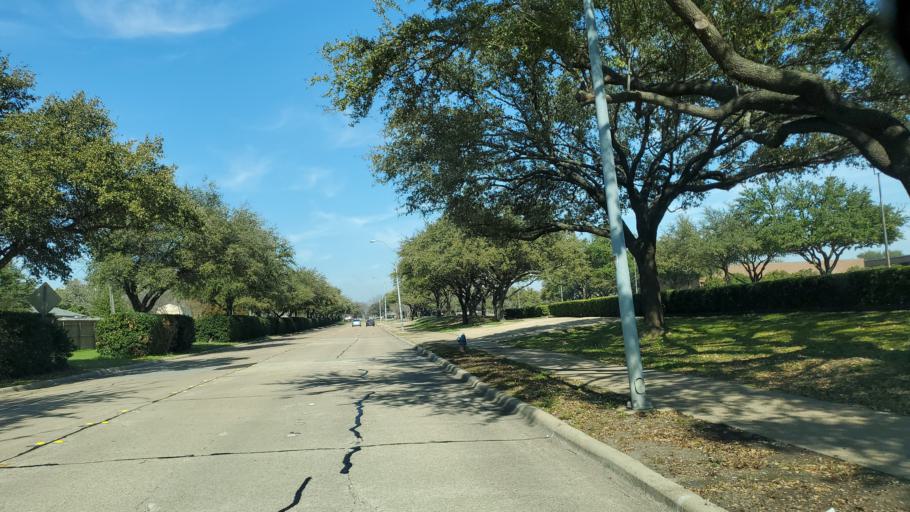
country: US
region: Texas
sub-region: Dallas County
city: Richardson
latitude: 32.9626
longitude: -96.7285
